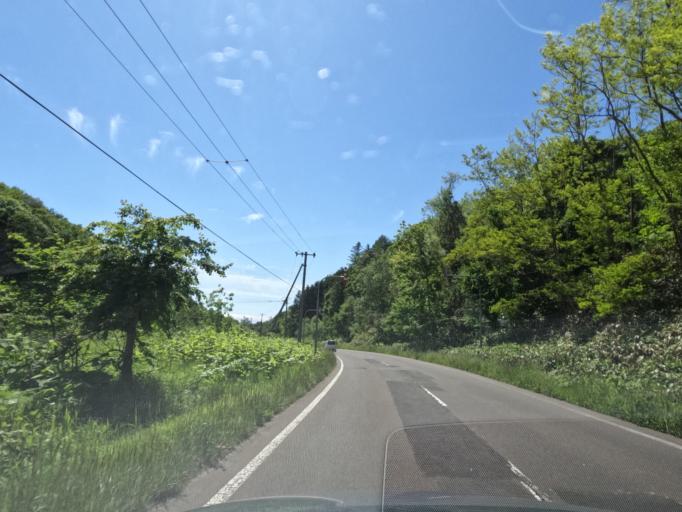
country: JP
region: Hokkaido
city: Iwamizawa
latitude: 43.1013
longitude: 141.7762
